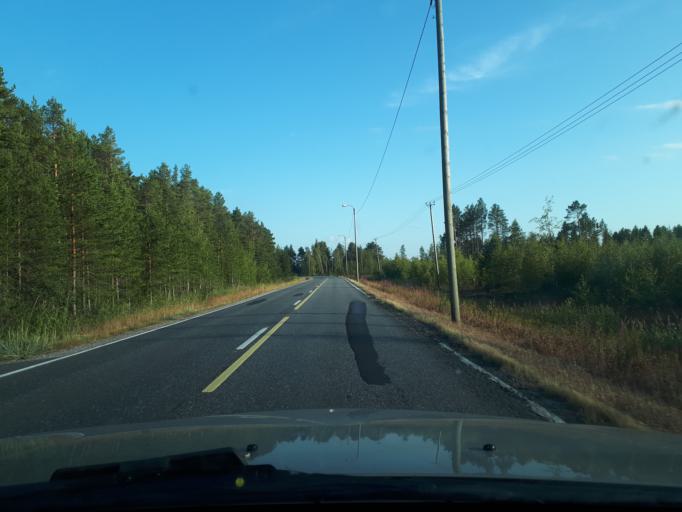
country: FI
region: Northern Ostrobothnia
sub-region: Oulu
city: Oulunsalo
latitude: 64.9907
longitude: 25.2574
